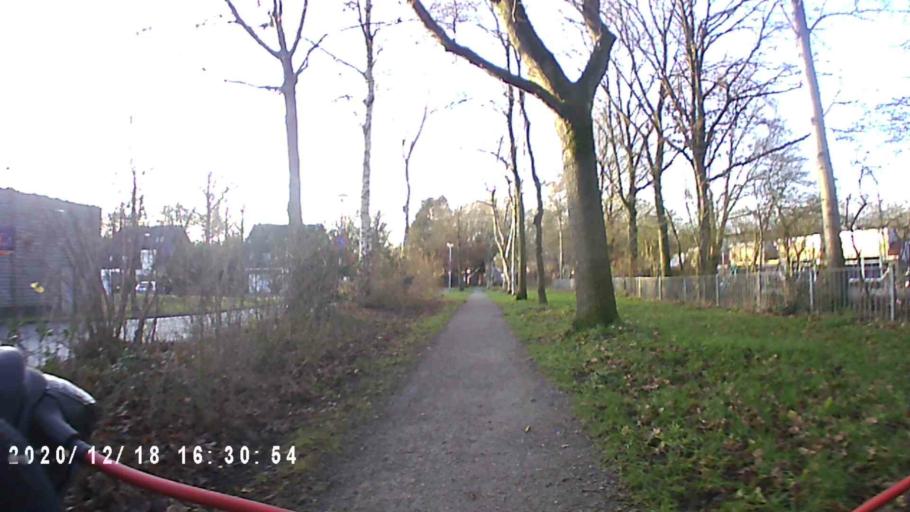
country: NL
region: Drenthe
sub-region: Gemeente Tynaarlo
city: Zuidlaren
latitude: 53.0779
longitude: 6.6988
